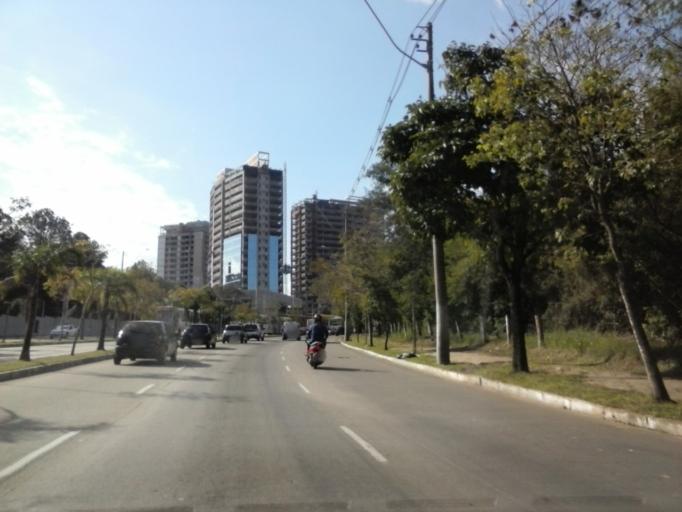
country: BR
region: Rio Grande do Sul
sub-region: Porto Alegre
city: Porto Alegre
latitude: -30.0455
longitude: -51.1772
